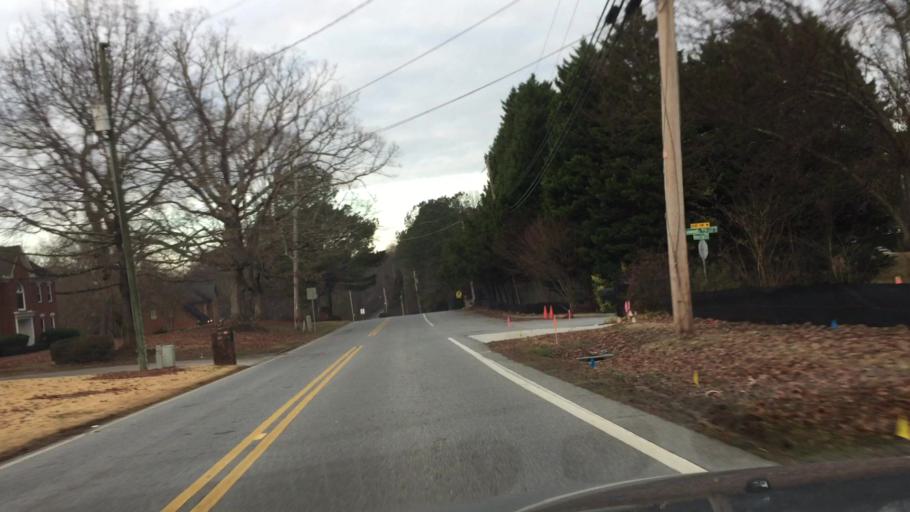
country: US
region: Georgia
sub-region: DeKalb County
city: Doraville
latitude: 33.9550
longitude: -84.2742
